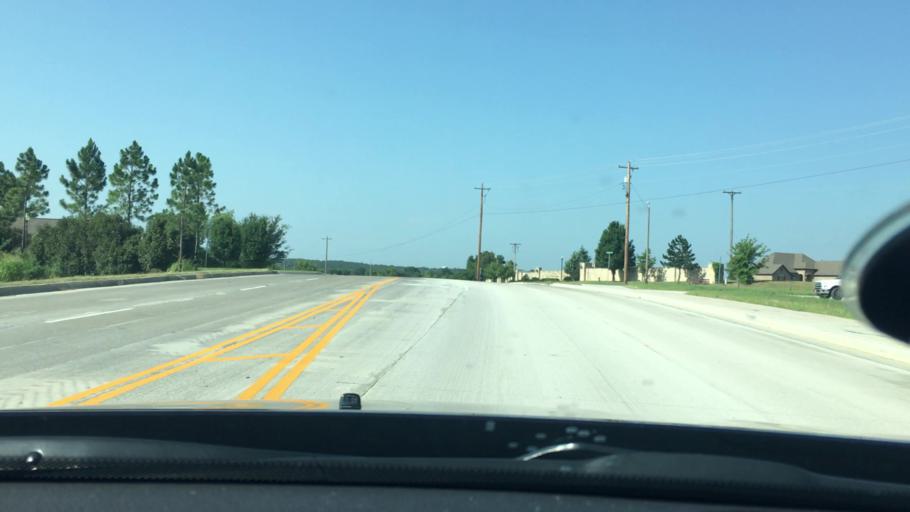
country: US
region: Oklahoma
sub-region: Pontotoc County
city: Ada
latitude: 34.7580
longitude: -96.6693
